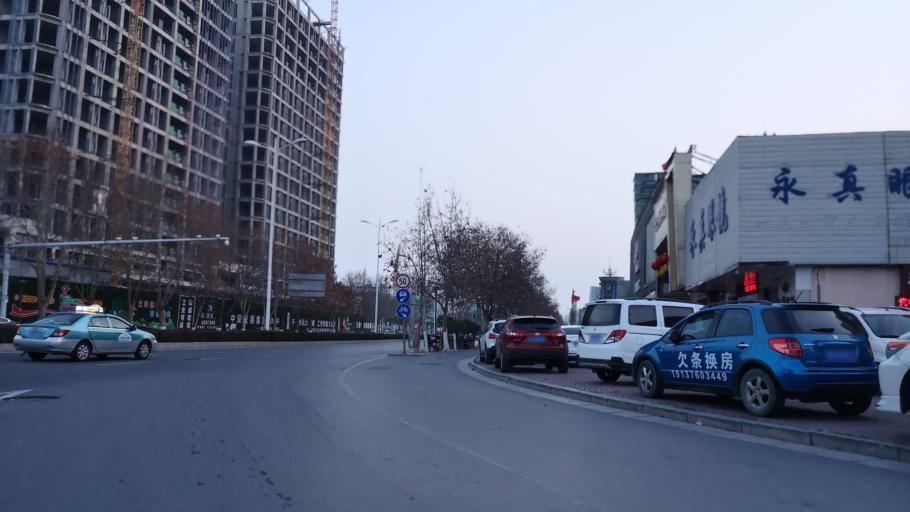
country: CN
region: Henan Sheng
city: Zhongyuanlu
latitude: 35.7764
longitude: 115.0704
